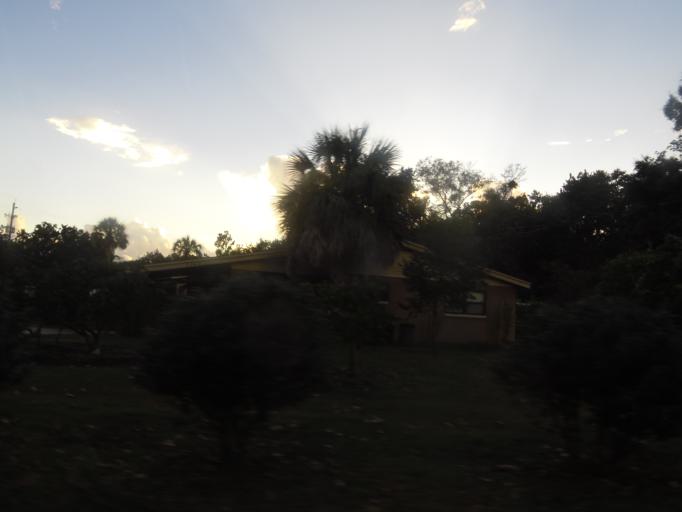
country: US
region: Florida
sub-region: Duval County
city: Jacksonville
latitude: 30.2323
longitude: -81.6134
